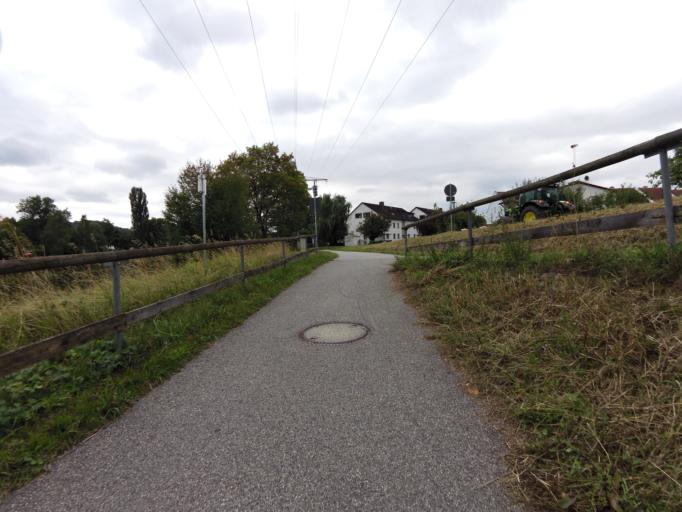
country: DE
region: Bavaria
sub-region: Lower Bavaria
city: Landshut
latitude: 48.5514
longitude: 12.1698
